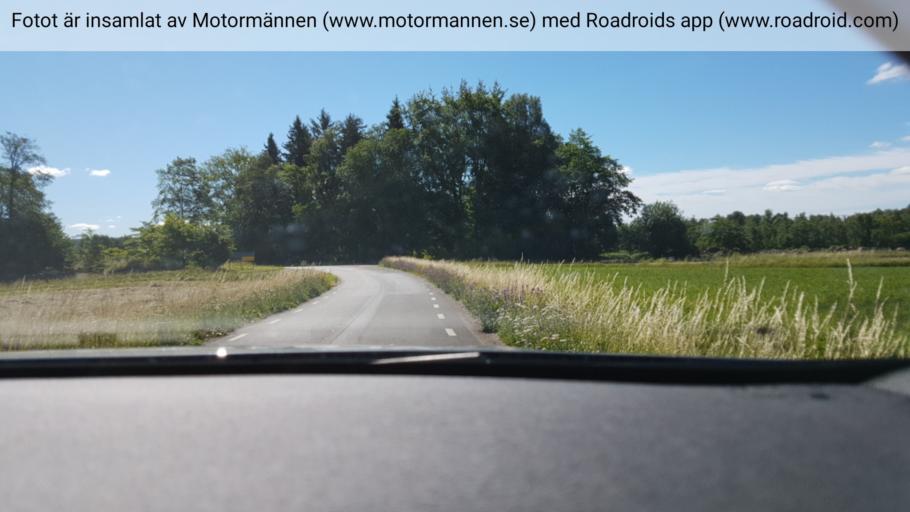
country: SE
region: Vaestra Goetaland
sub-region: Falkopings Kommun
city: Akarp
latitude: 58.2599
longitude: 13.6535
